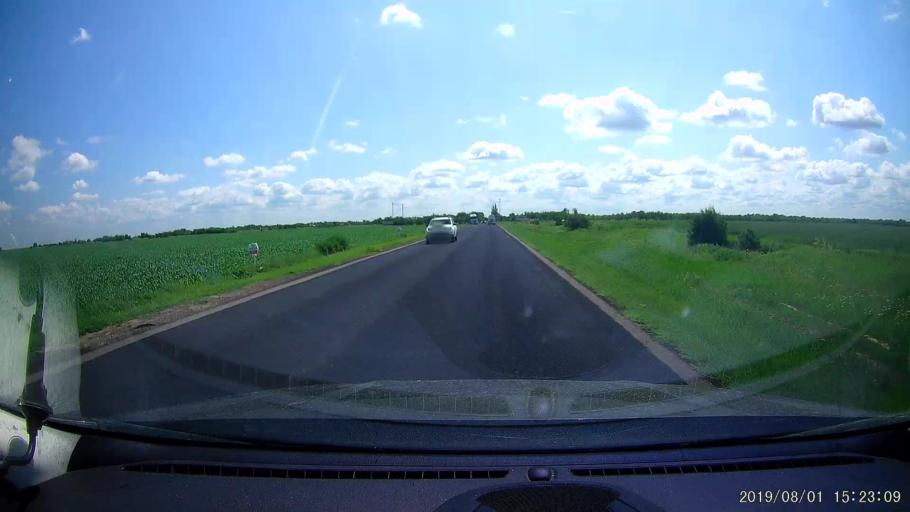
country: RO
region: Braila
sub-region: Comuna Viziru
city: Lanurile
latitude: 45.0442
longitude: 27.7643
